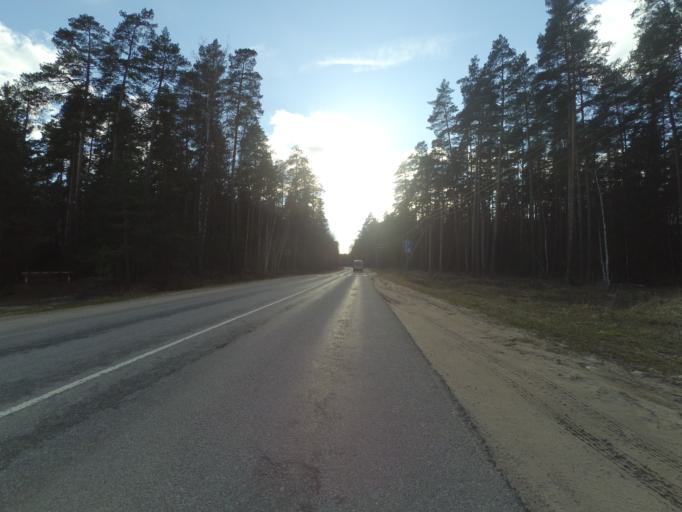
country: RU
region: Moskovskaya
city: Pushchino
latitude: 54.9053
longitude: 37.7142
